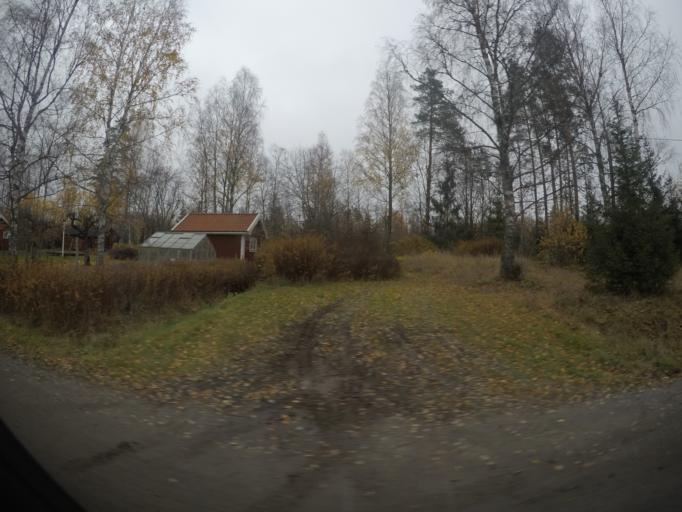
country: SE
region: Vaestmanland
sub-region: Surahammars Kommun
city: Ramnas
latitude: 59.7058
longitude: 16.0915
